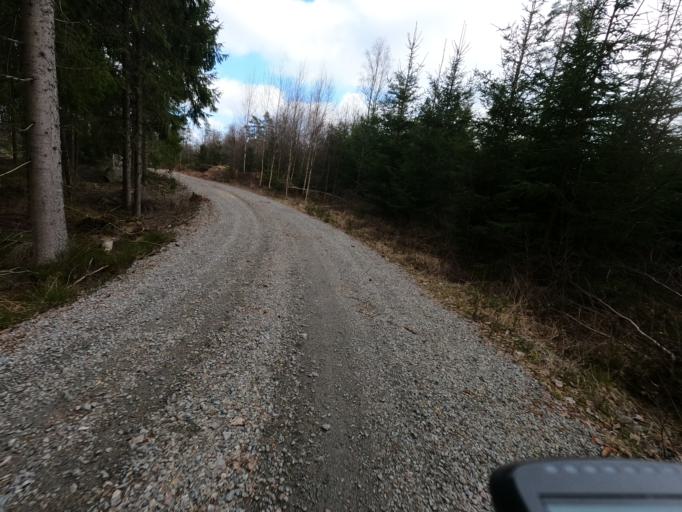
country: SE
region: Kronoberg
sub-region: Alvesta Kommun
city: Vislanda
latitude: 56.8109
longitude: 14.3892
